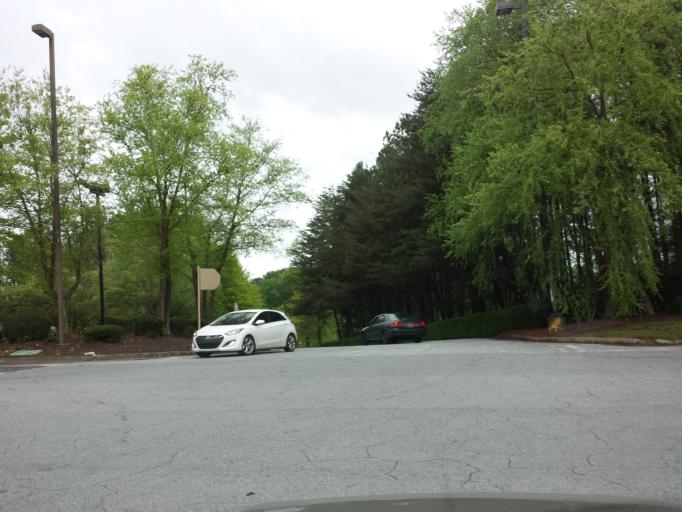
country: US
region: Georgia
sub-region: Cobb County
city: Kennesaw
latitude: 34.0008
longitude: -84.5858
